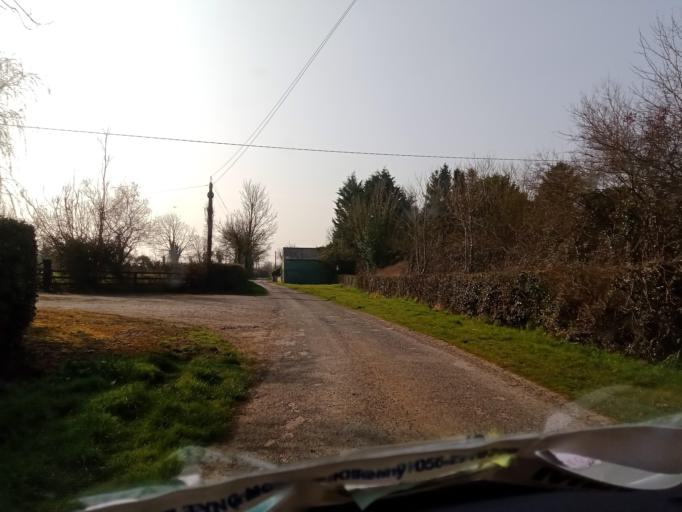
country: IE
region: Leinster
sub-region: Kilkenny
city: Callan
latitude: 52.5255
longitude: -7.4008
